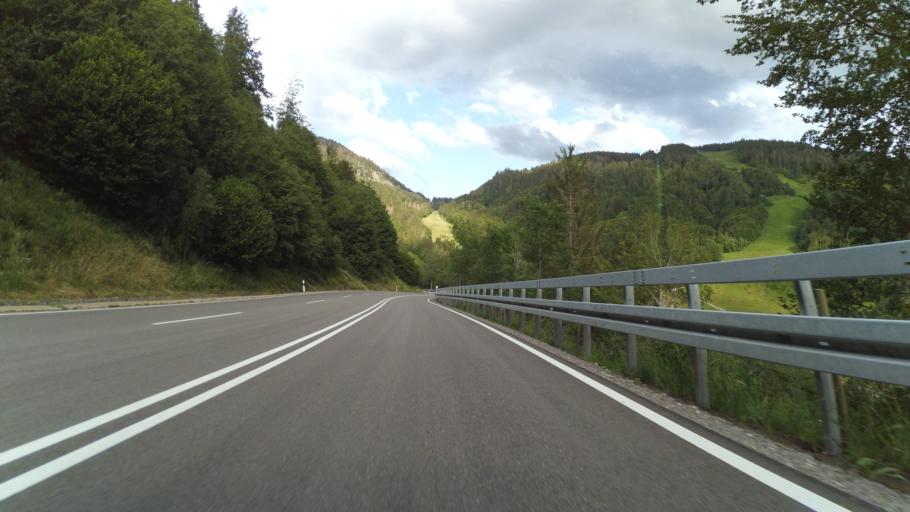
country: DE
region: Baden-Wuerttemberg
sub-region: Freiburg Region
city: Todtnau
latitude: 47.8579
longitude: 8.0015
